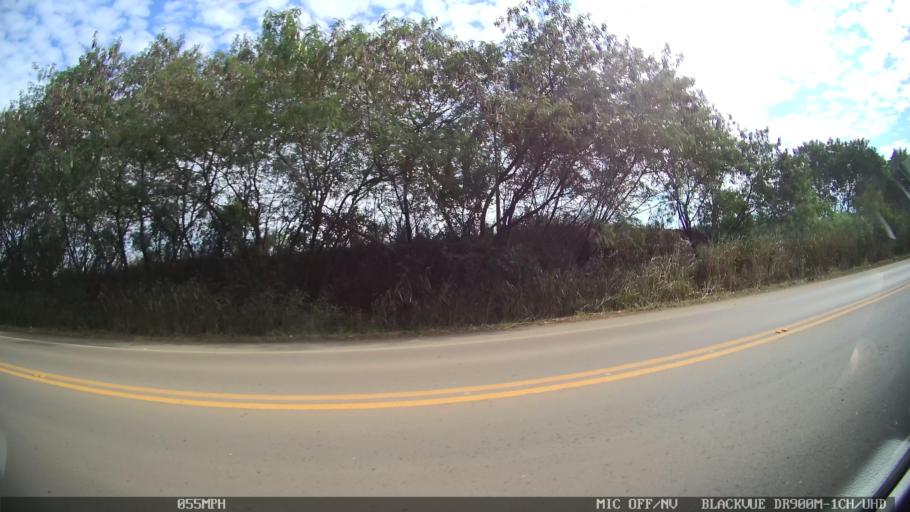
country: BR
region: Sao Paulo
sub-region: Santa Barbara D'Oeste
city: Santa Barbara d'Oeste
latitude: -22.7285
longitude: -47.4250
